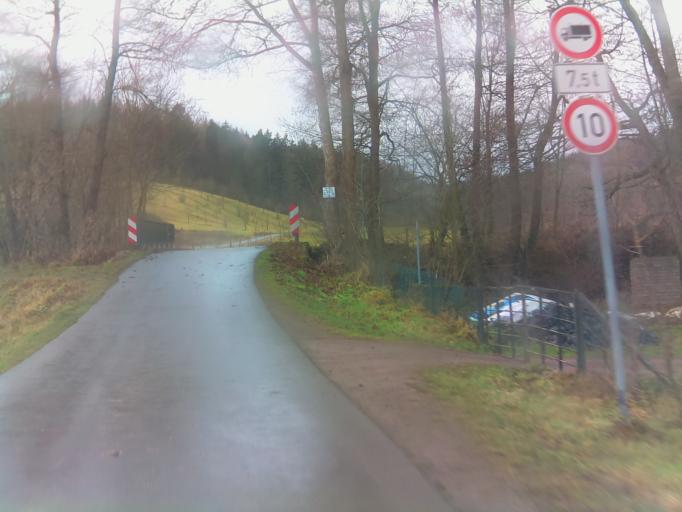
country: DE
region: Thuringia
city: Angelroda
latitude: 50.7393
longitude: 10.8590
